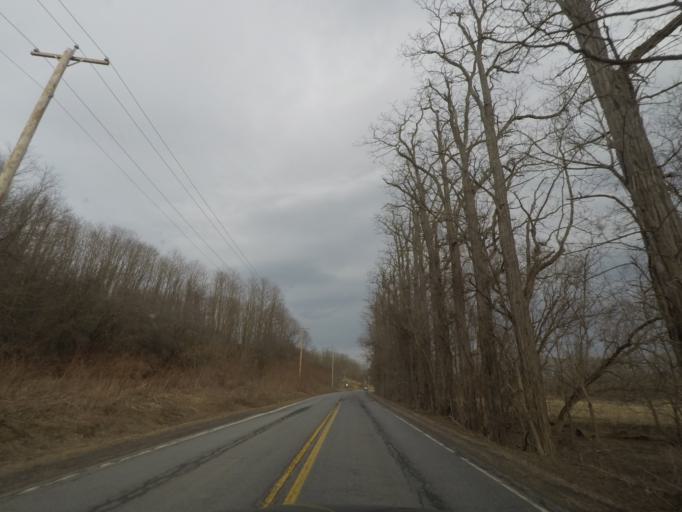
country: US
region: New York
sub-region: Washington County
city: Cambridge
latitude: 42.9578
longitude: -73.4396
